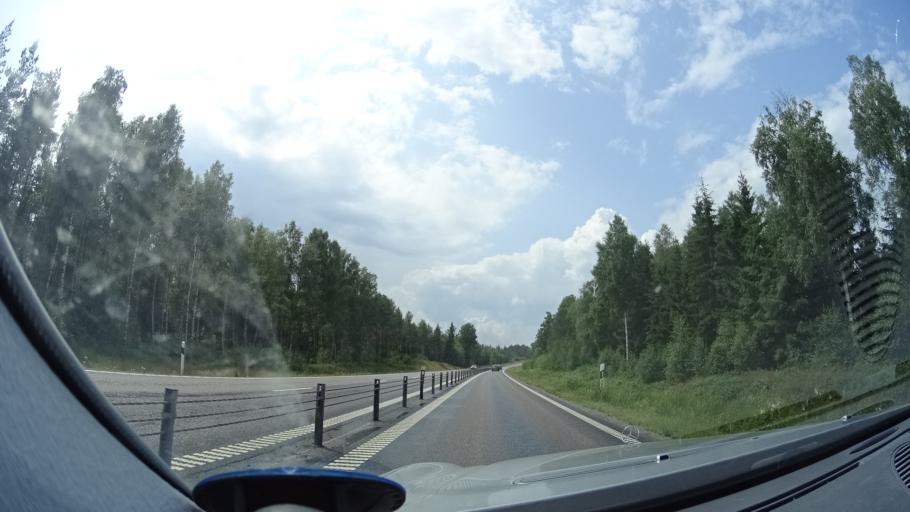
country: SE
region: Kalmar
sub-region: Nybro Kommun
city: Nybro
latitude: 56.7260
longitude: 15.8233
